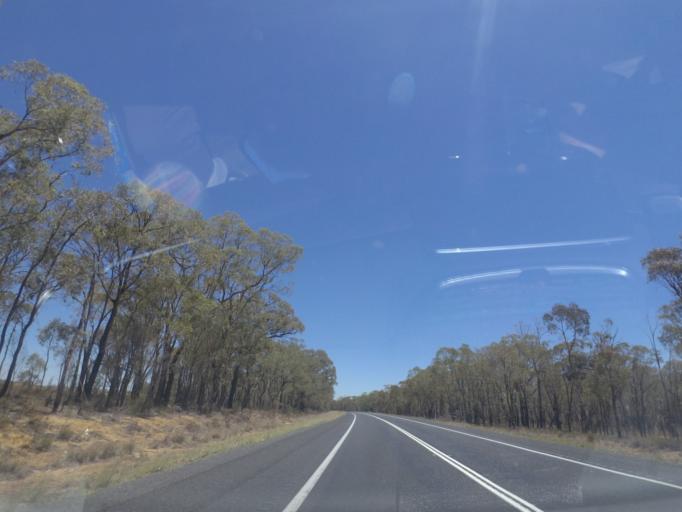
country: AU
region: New South Wales
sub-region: Warrumbungle Shire
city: Coonabarabran
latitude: -31.2062
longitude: 149.3338
